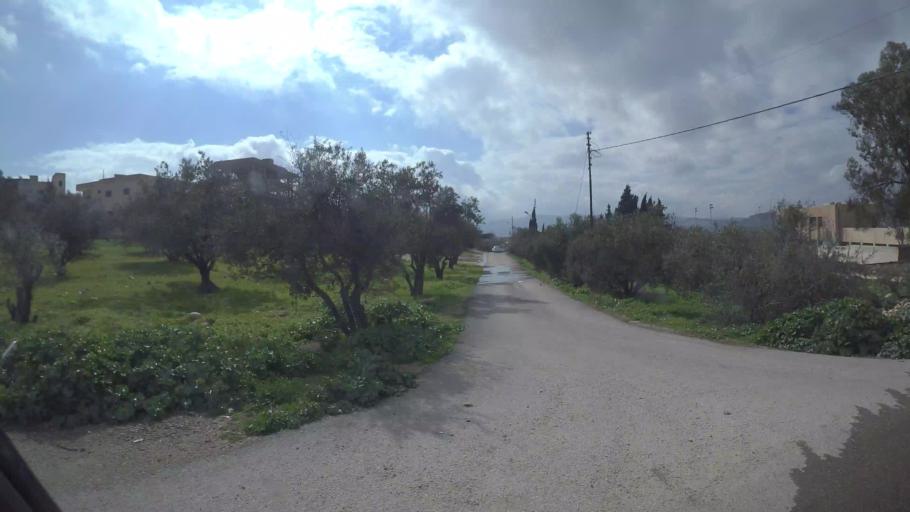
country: JO
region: Amman
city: Al Jubayhah
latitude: 32.0760
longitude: 35.8626
